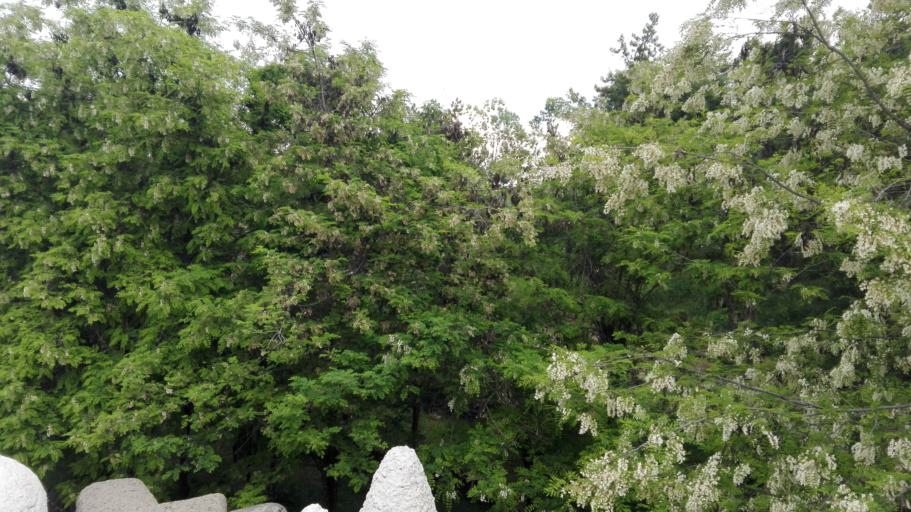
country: TR
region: Batman
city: Batman
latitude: 37.9080
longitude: 41.1309
